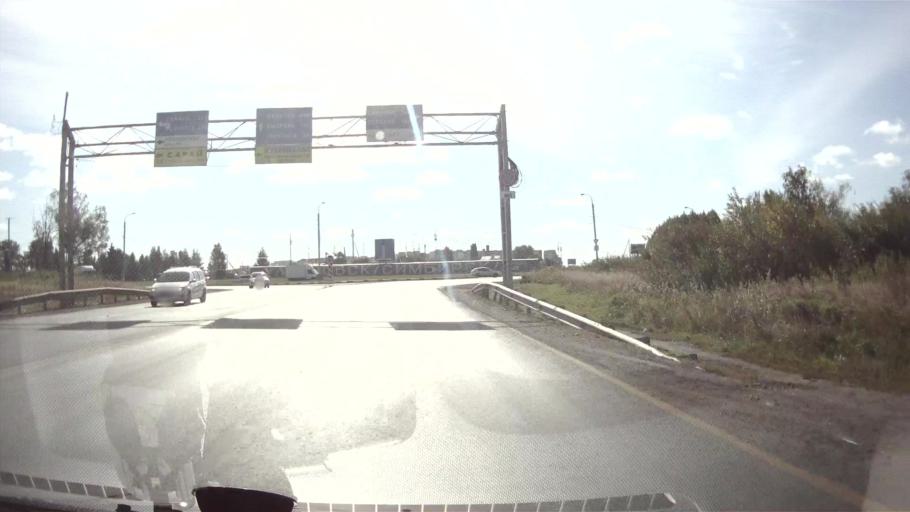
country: RU
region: Ulyanovsk
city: Isheyevka
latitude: 54.2922
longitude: 48.2533
